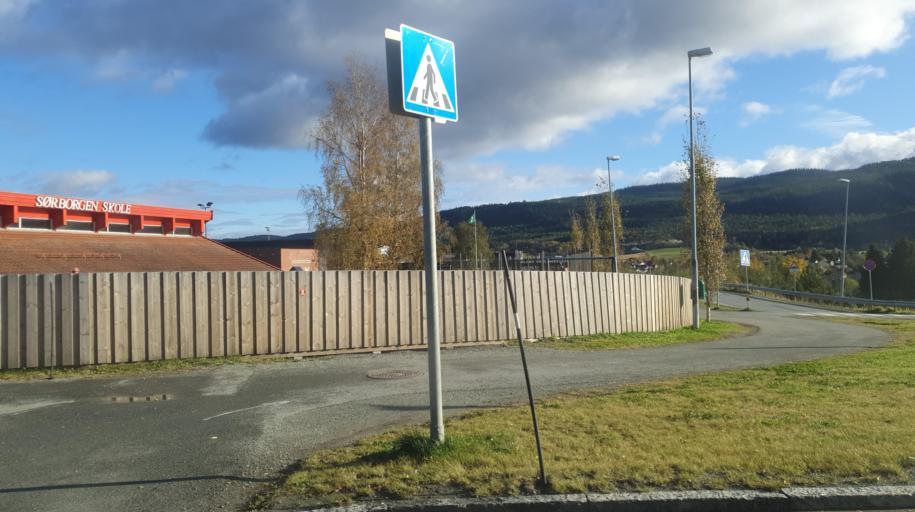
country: NO
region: Sor-Trondelag
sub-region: Klaebu
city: Klaebu
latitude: 63.3046
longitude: 10.4611
